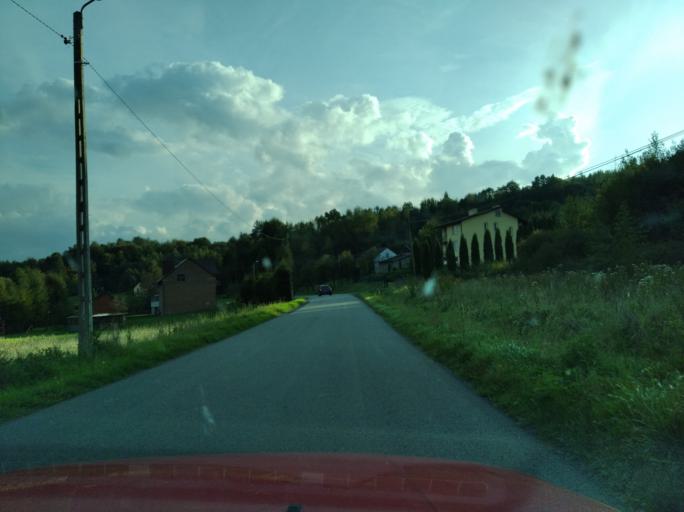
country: PL
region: Subcarpathian Voivodeship
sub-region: Powiat przemyski
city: Nienadowa
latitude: 49.8546
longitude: 22.4232
